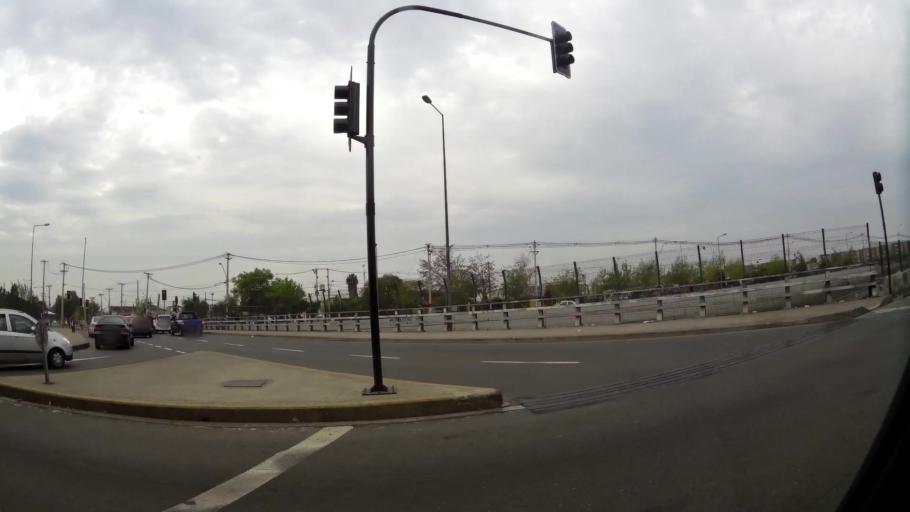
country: CL
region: Santiago Metropolitan
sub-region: Provincia de Santiago
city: Lo Prado
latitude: -33.4984
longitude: -70.7446
